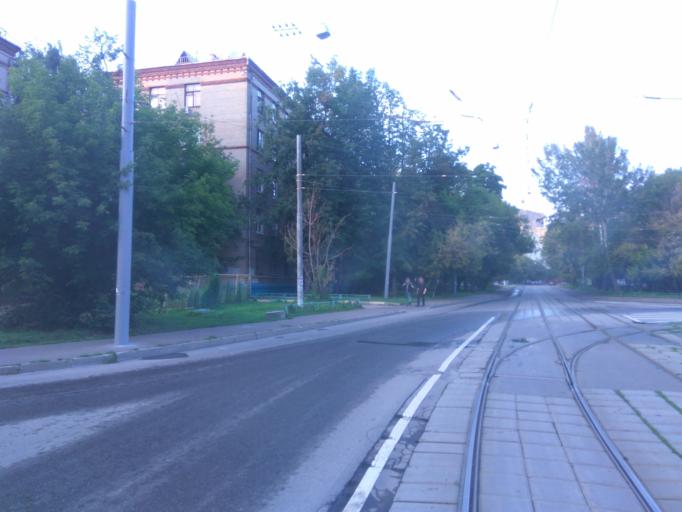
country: RU
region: Moskovskaya
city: Bogorodskoye
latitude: 55.8174
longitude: 37.7015
